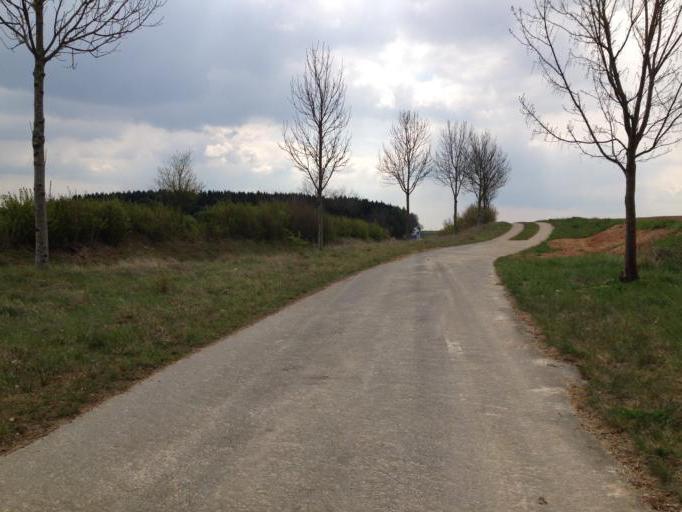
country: DE
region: Hesse
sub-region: Regierungsbezirk Giessen
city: Grunberg
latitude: 50.6302
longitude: 8.9832
